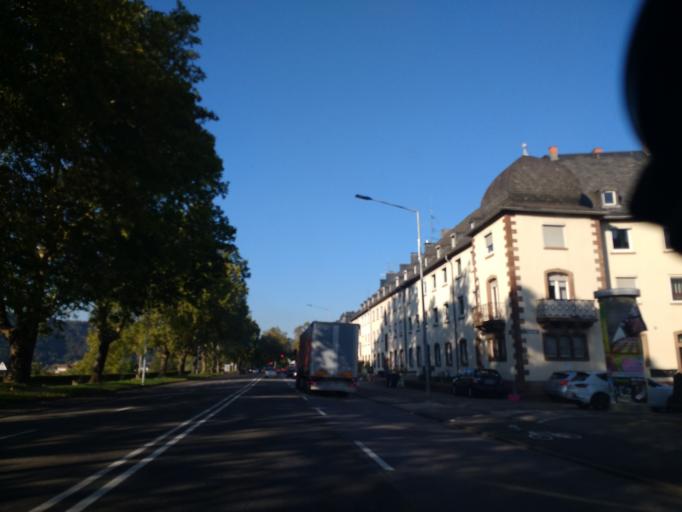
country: DE
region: Rheinland-Pfalz
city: Trier
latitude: 49.7428
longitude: 6.6284
